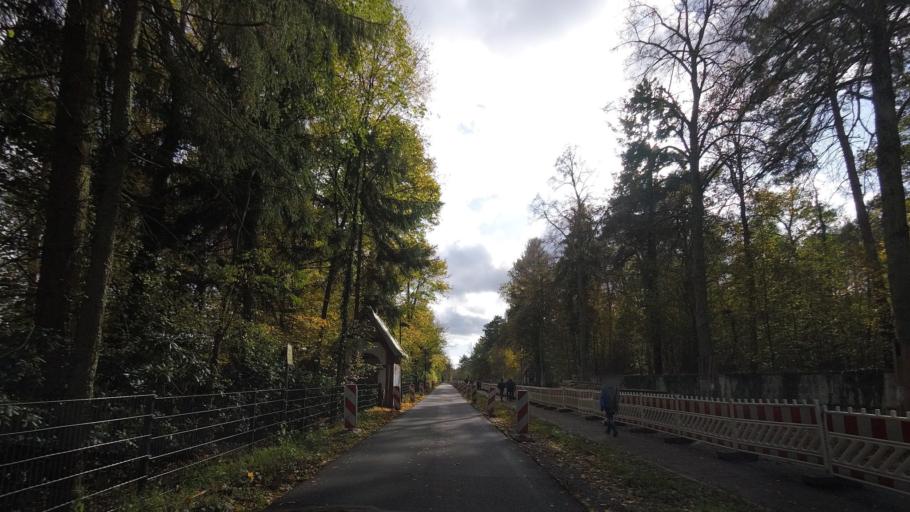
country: DE
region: Brandenburg
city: Fichtenwalde
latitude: 52.2644
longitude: 12.9225
